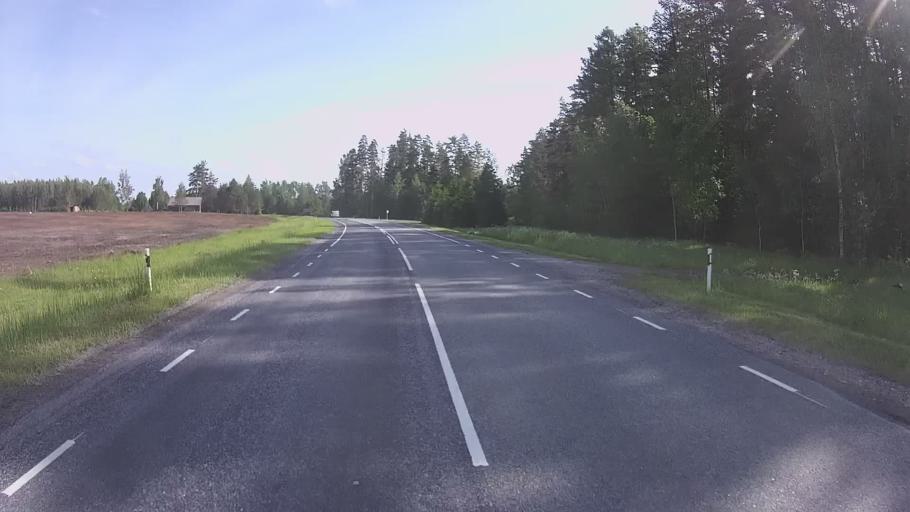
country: EE
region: Valgamaa
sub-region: Torva linn
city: Torva
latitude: 58.0324
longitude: 25.9699
